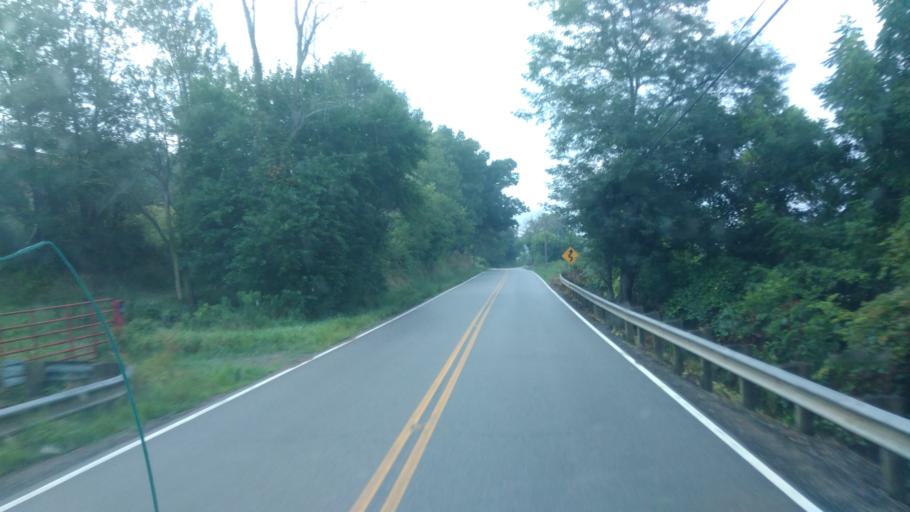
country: US
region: Ohio
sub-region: Guernsey County
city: Byesville
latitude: 39.9754
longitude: -81.5365
